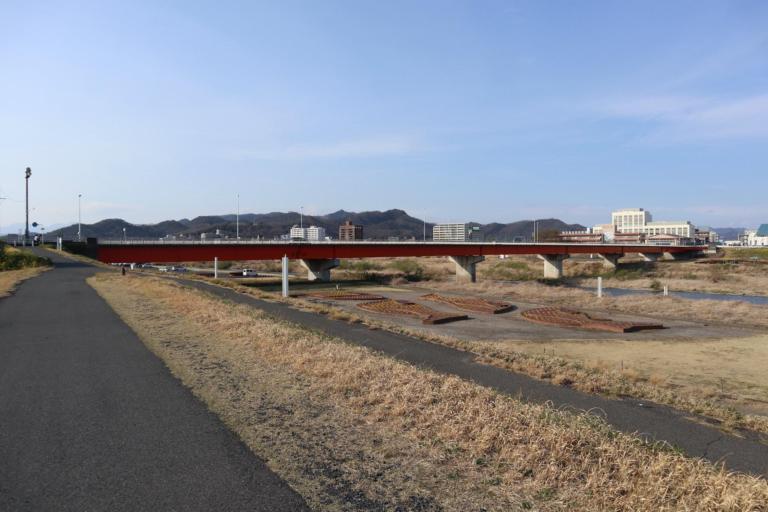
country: JP
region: Tochigi
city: Ashikaga
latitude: 36.3273
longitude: 139.4534
